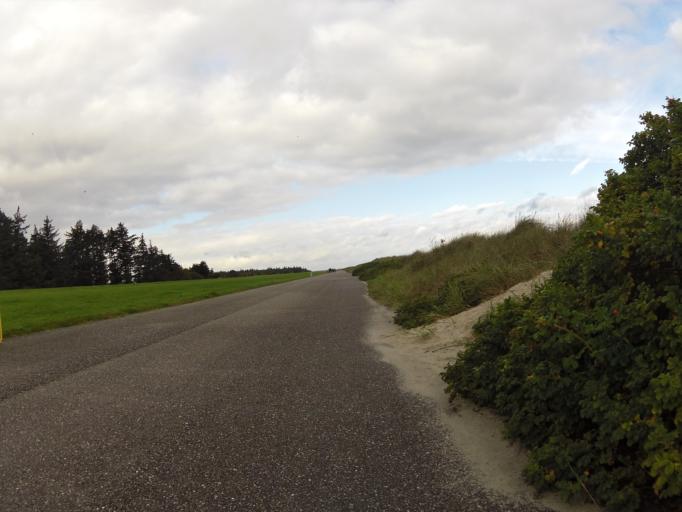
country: DE
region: Schleswig-Holstein
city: Wisch
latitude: 54.4314
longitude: 10.3562
